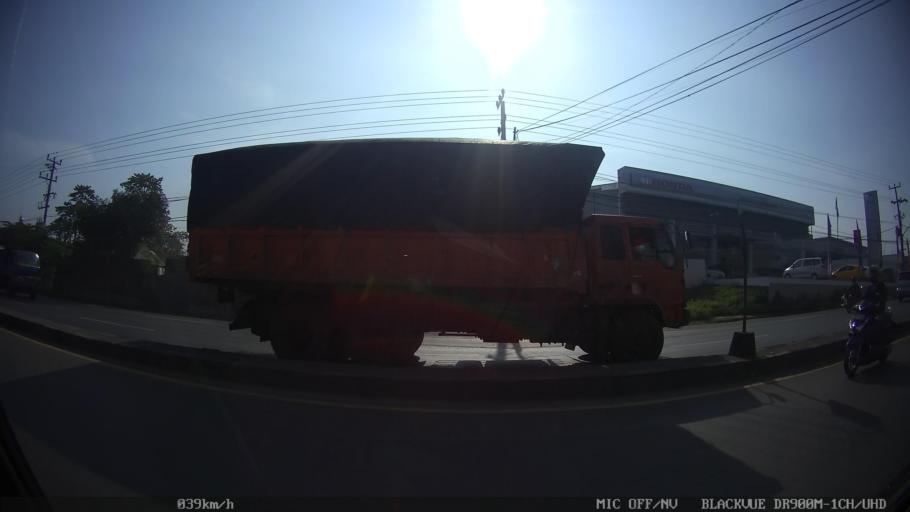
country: ID
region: Lampung
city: Natar
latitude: -5.3512
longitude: 105.2183
